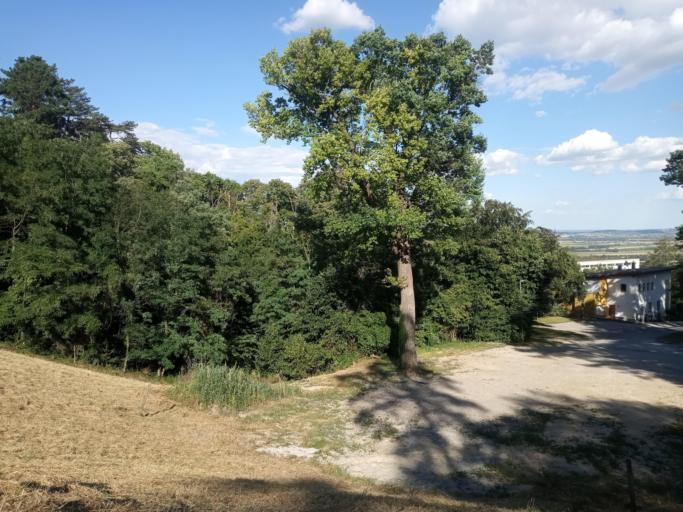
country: AT
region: Burgenland
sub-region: Eisenstadt Stadt
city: Eisenstadt
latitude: 47.8538
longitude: 16.5097
